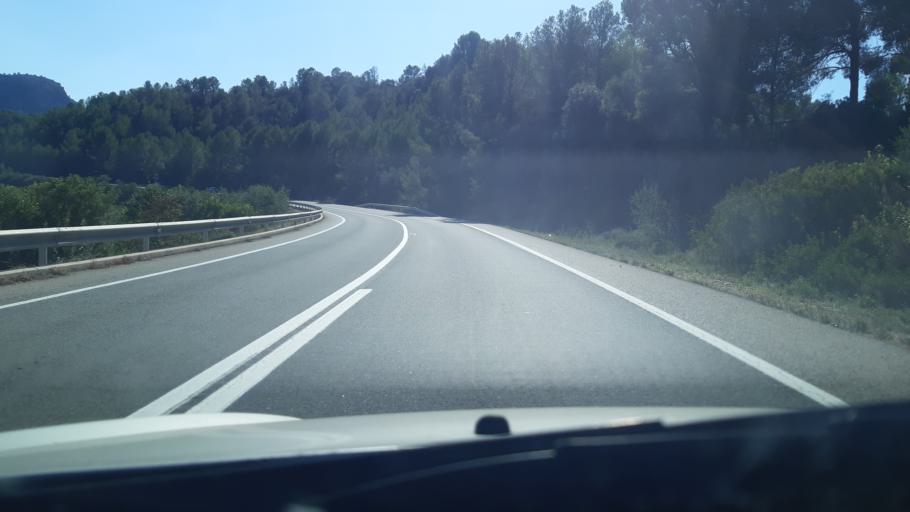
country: ES
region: Catalonia
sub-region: Provincia de Tarragona
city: Benifallet
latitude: 40.9473
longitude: 0.4833
